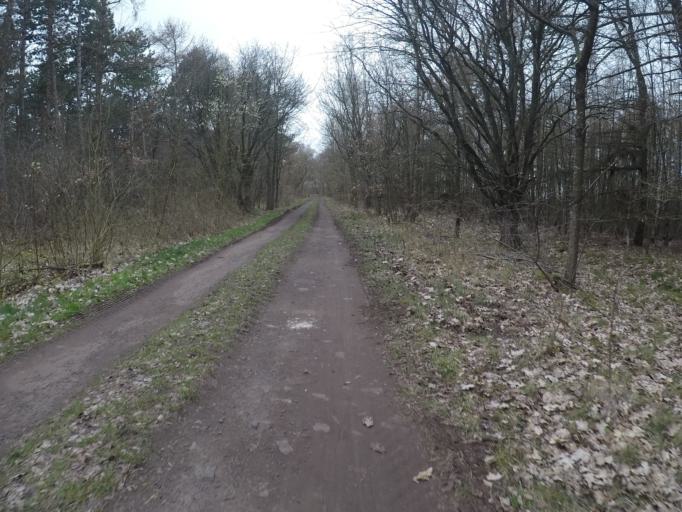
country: DE
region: Lower Saxony
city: Nordholz
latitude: 53.8273
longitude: 8.6013
